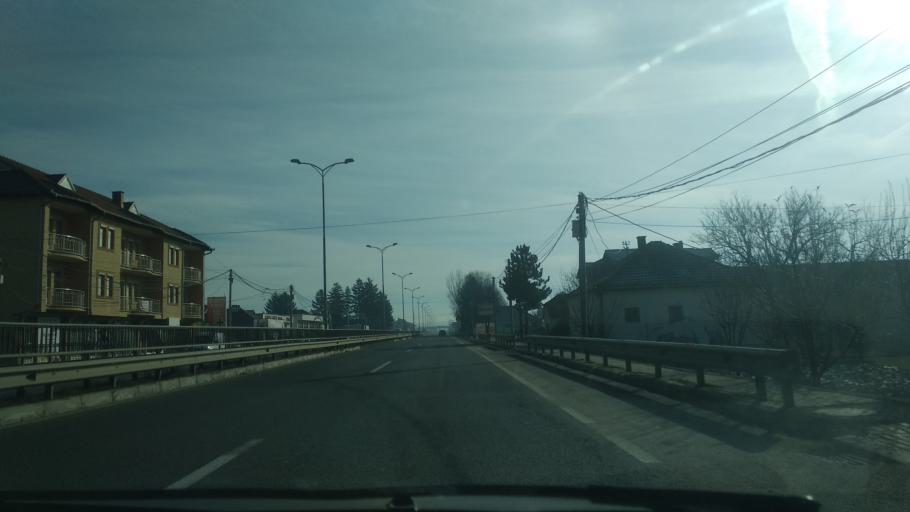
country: XK
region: Pristina
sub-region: Komuna e Obiliqit
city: Obiliq
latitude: 42.7222
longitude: 21.0851
